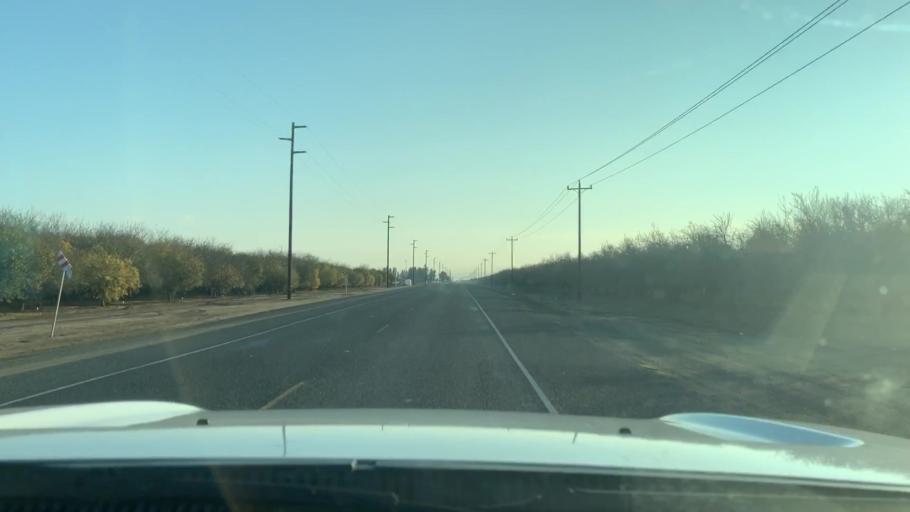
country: US
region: California
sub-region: Kern County
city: Lost Hills
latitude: 35.6011
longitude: -119.5212
